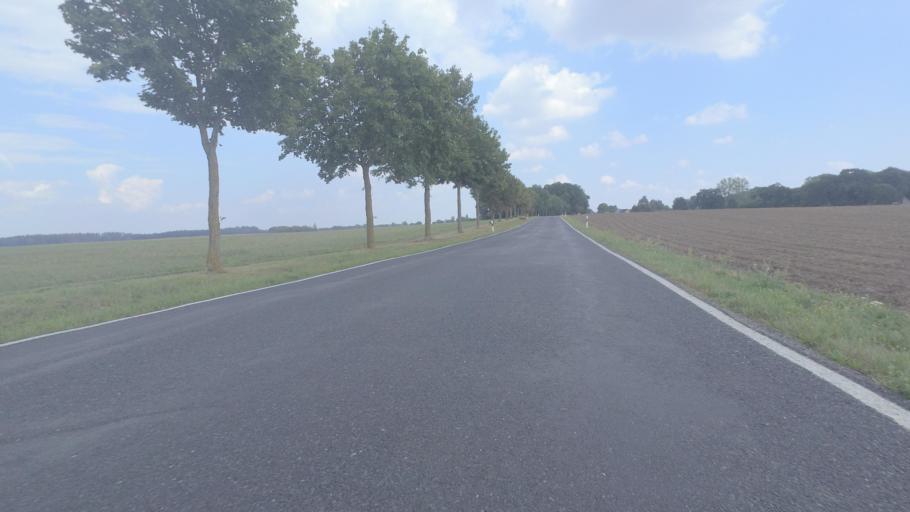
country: DE
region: Mecklenburg-Vorpommern
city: Borrentin
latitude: 53.8504
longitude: 12.9930
